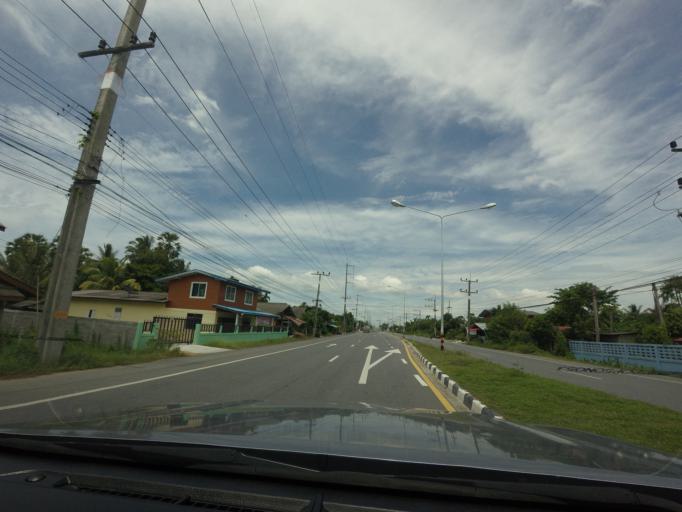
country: TH
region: Songkhla
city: Krasae Sin
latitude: 7.6913
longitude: 100.3776
